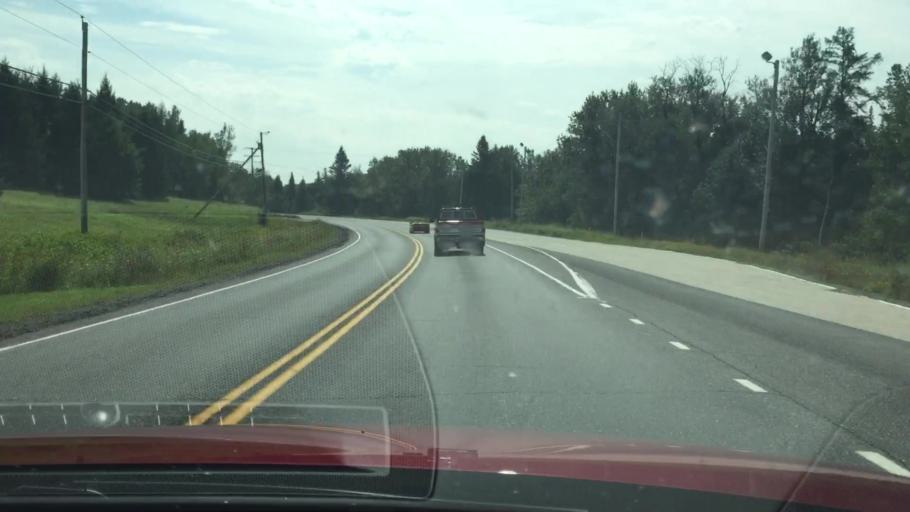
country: US
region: Maine
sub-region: Aroostook County
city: Presque Isle
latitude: 46.6227
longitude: -67.9898
